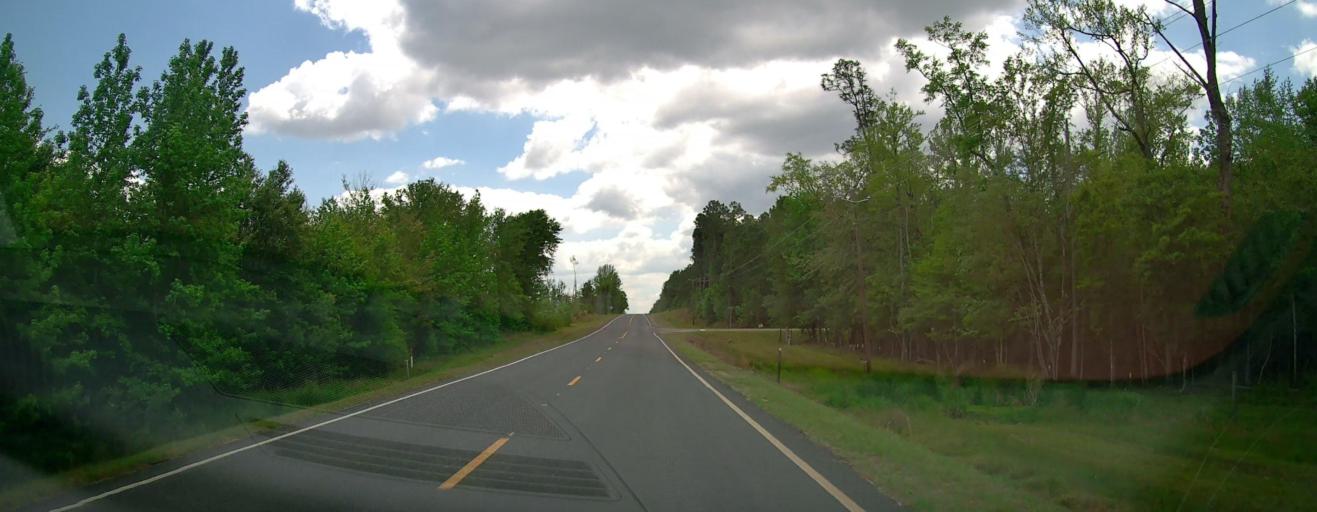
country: US
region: Georgia
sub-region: Treutlen County
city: Soperton
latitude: 32.4687
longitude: -82.6024
